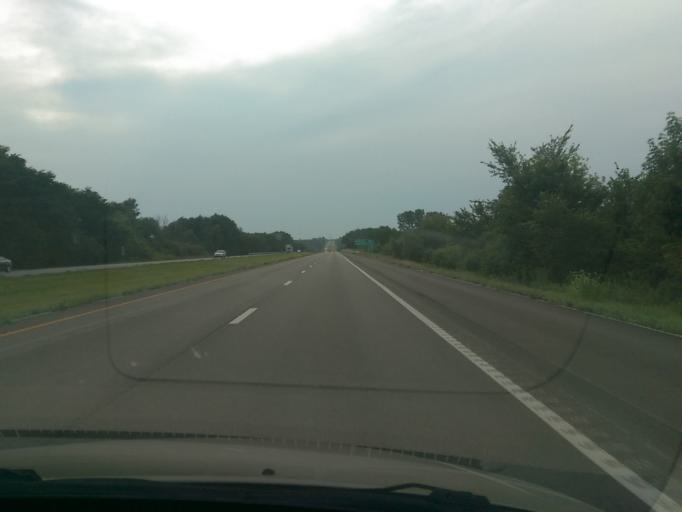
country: US
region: Missouri
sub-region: Andrew County
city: Savannah
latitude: 39.8942
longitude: -94.8689
